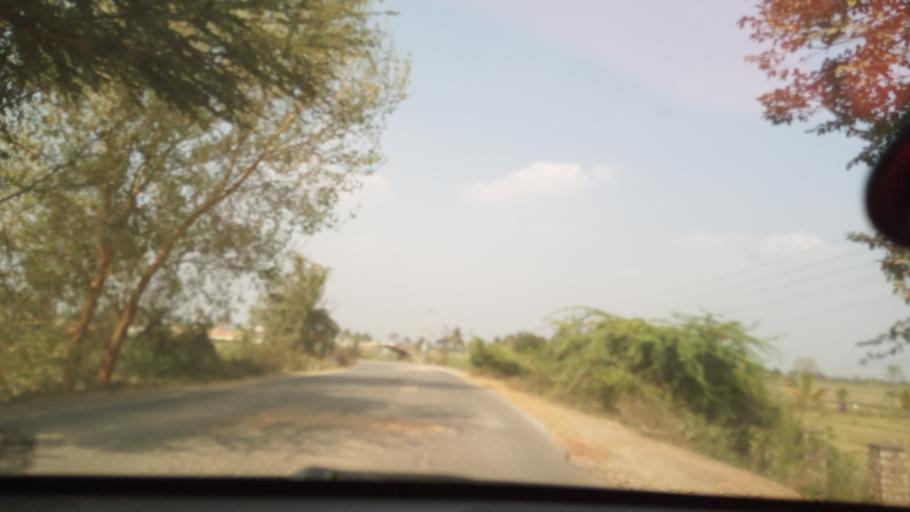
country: IN
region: Karnataka
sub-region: Mysore
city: Nanjangud
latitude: 12.1103
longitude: 76.7048
